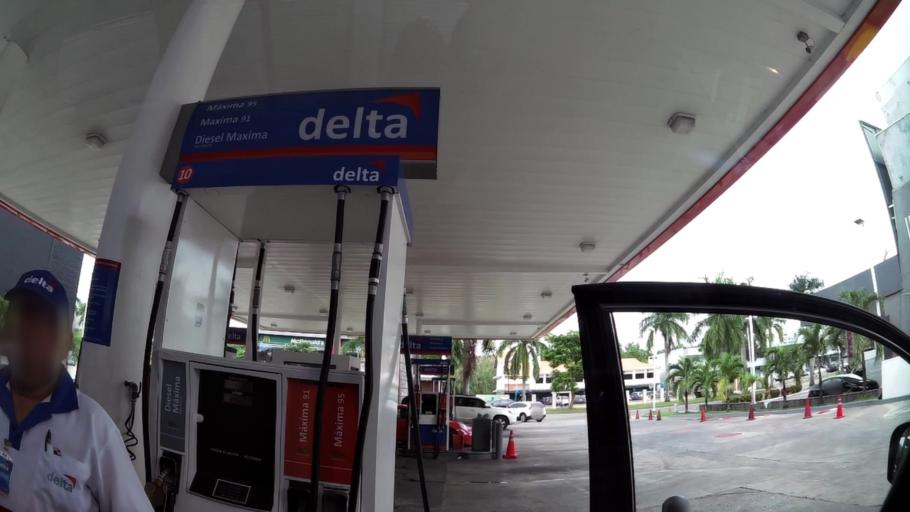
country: PA
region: Panama
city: San Miguelito
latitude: 9.0152
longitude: -79.4740
